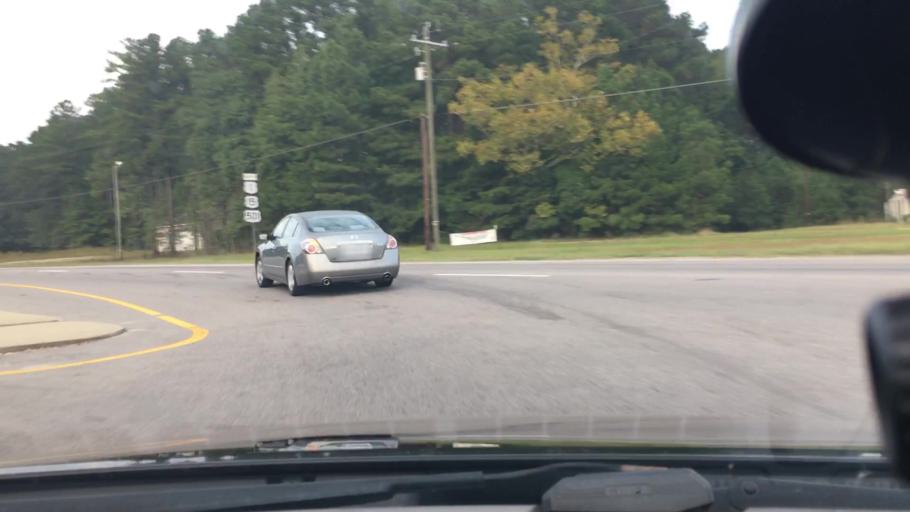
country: US
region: North Carolina
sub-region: Lee County
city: Sanford
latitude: 35.4040
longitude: -79.2315
